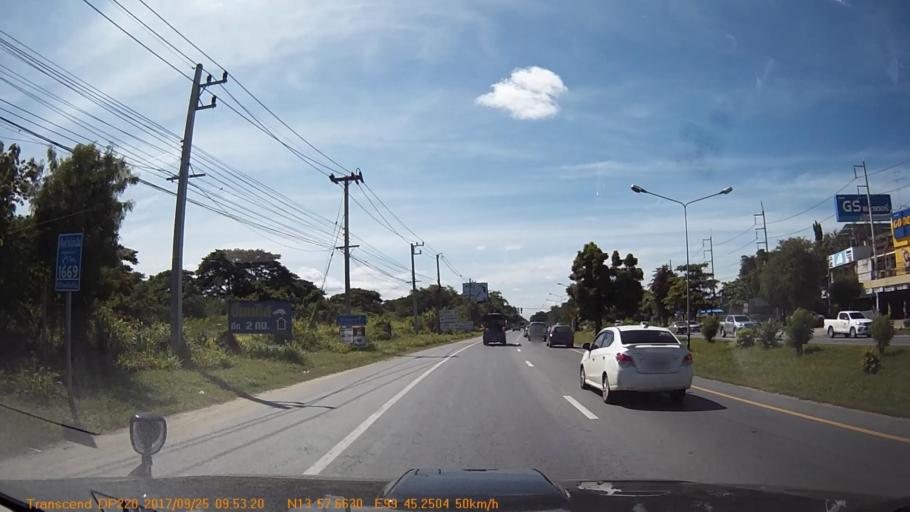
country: TH
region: Kanchanaburi
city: Tha Maka
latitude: 13.9609
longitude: 99.7542
